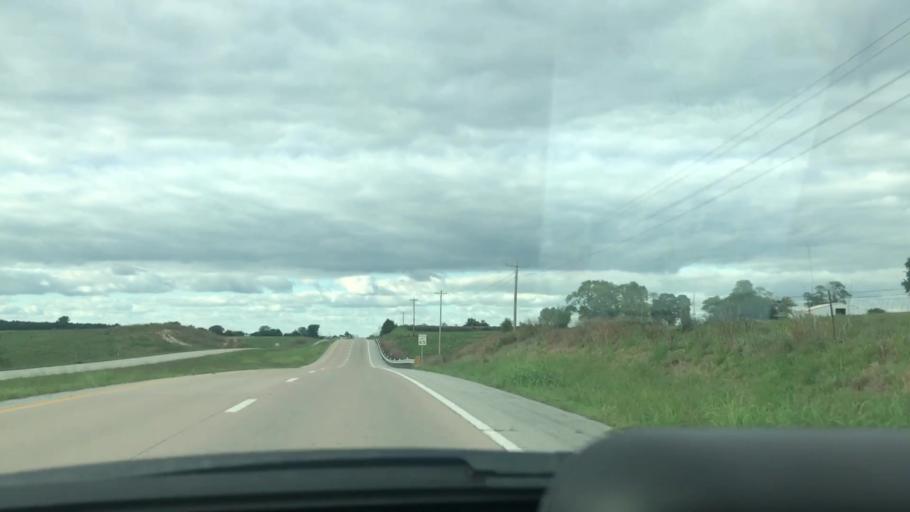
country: US
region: Missouri
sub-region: Benton County
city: Lincoln
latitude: 38.3205
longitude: -93.3421
